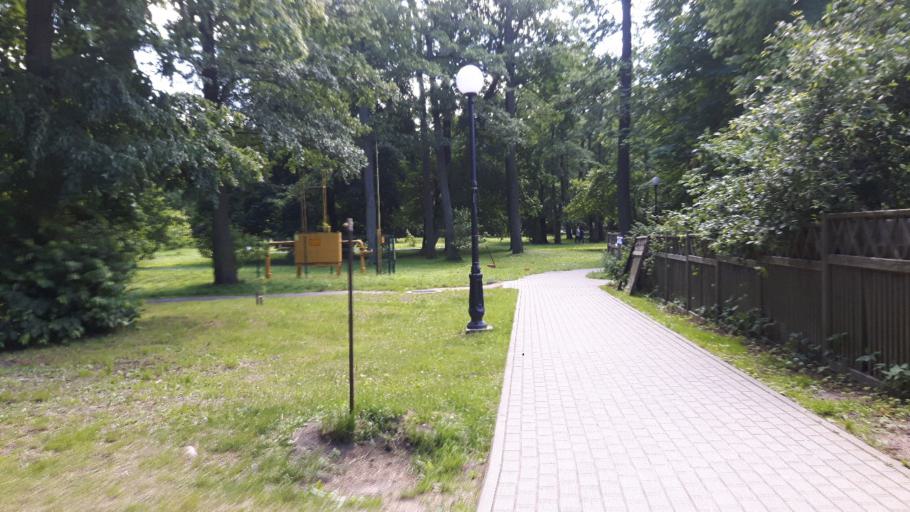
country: RU
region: Kaliningrad
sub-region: Zelenogradskiy Rayon
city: Zelenogradsk
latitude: 54.9634
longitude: 20.4864
